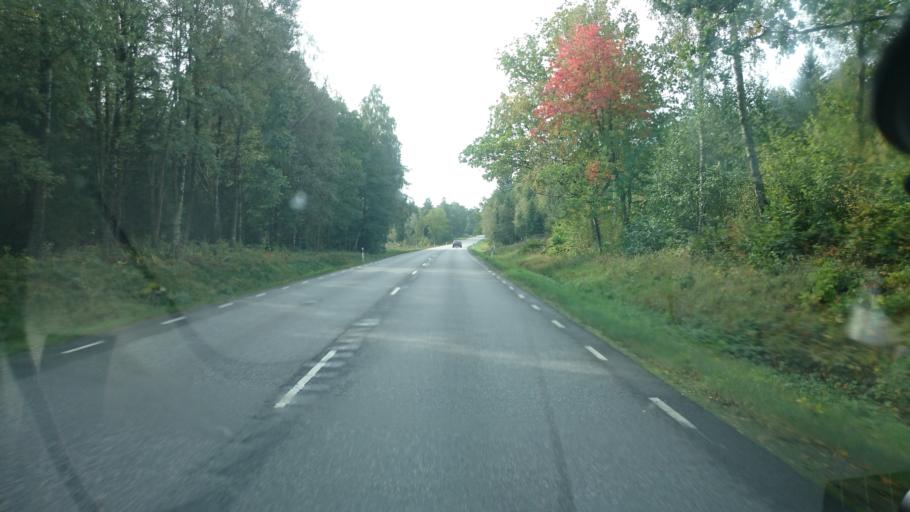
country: SE
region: Vaestra Goetaland
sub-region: Alingsas Kommun
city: Alingsas
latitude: 58.0160
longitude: 12.4524
